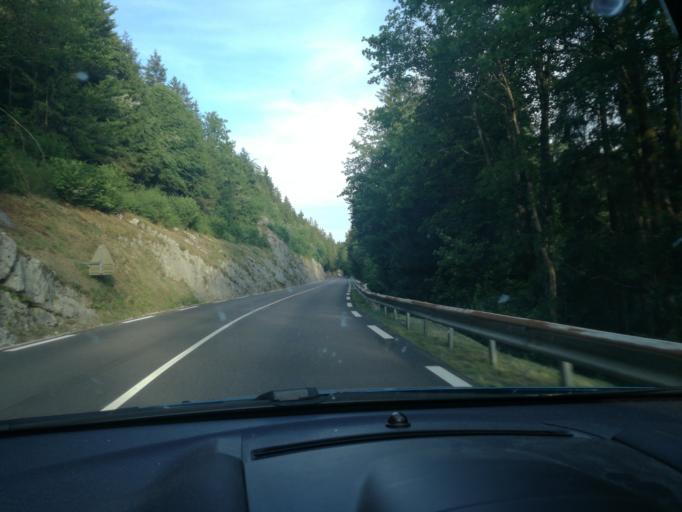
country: FR
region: Franche-Comte
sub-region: Departement du Jura
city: Morbier
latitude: 46.6261
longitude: 5.9543
